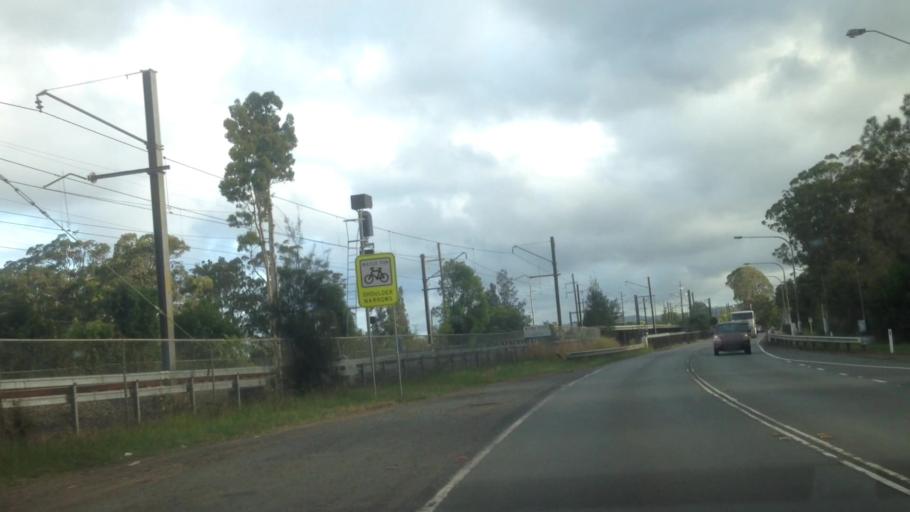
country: AU
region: New South Wales
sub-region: Wyong Shire
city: Chittaway Bay
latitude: -33.2896
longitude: 151.4242
